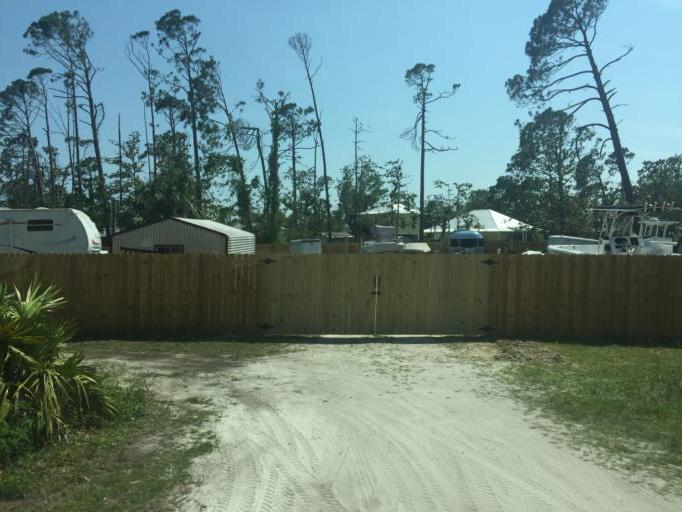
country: US
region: Florida
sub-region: Bay County
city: Upper Grand Lagoon
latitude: 30.1573
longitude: -85.7240
